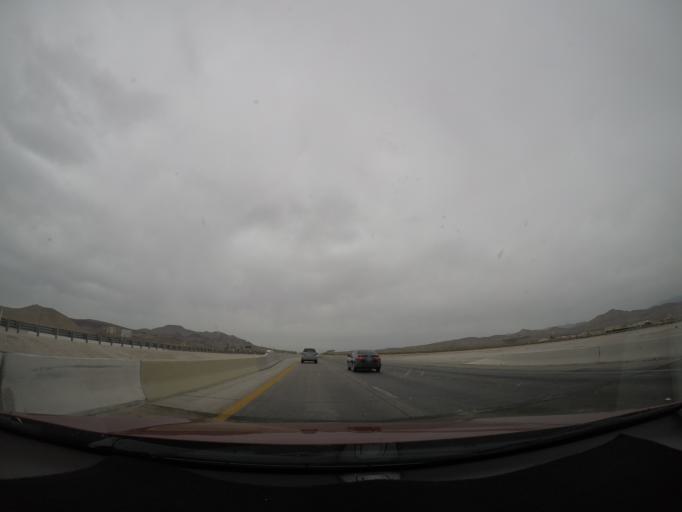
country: US
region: Nevada
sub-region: Clark County
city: Enterprise
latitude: 35.9305
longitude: -115.1933
